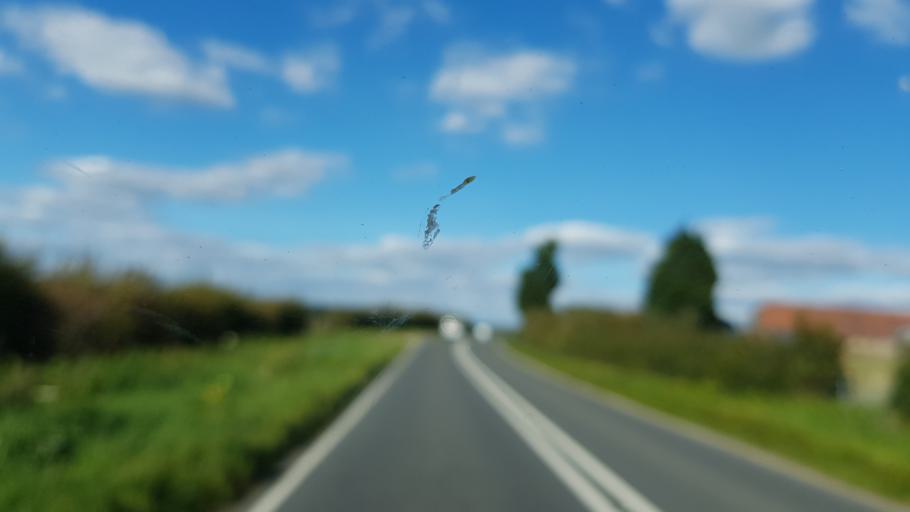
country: GB
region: England
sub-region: West Sussex
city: Petworth
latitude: 51.0395
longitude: -0.6406
